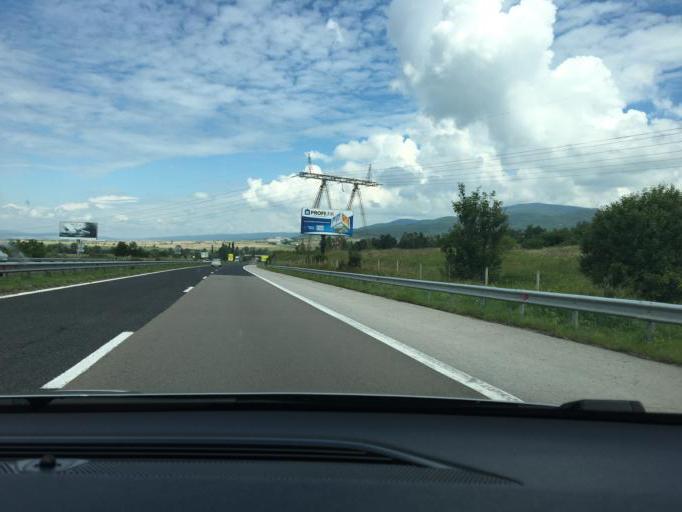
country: BG
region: Sofiya
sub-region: Obshtina Ikhtiman
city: Ikhtiman
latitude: 42.3927
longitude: 23.8716
